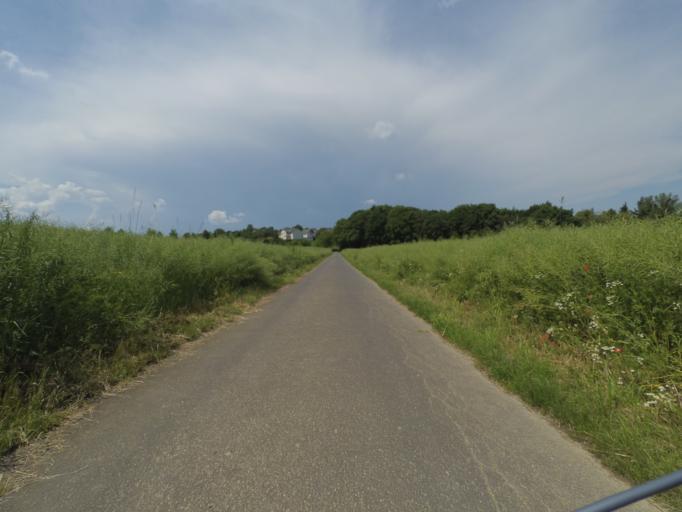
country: DE
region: Rheinland-Pfalz
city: Beulich
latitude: 50.1708
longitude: 7.4576
